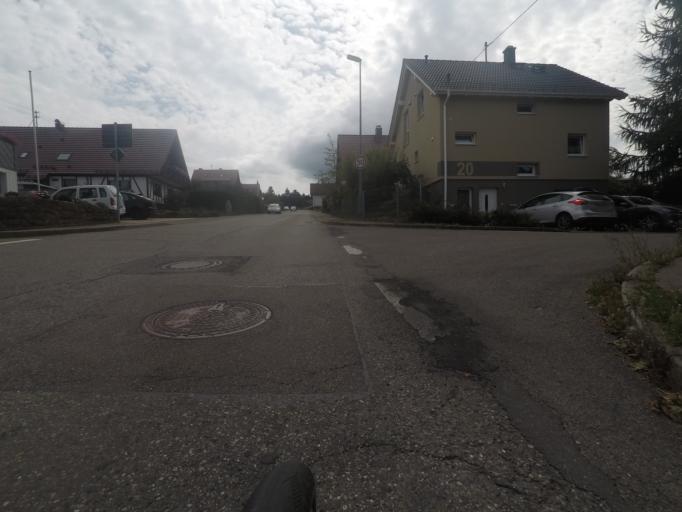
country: DE
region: Baden-Wuerttemberg
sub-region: Karlsruhe Region
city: Dobel
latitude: 48.8160
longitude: 8.4815
